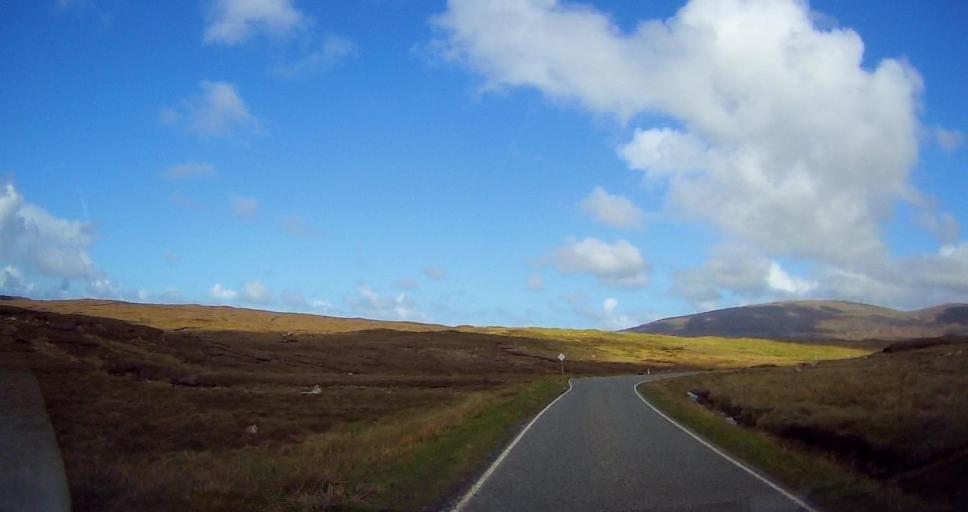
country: GB
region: Scotland
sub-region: Shetland Islands
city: Lerwick
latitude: 60.4962
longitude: -1.3936
